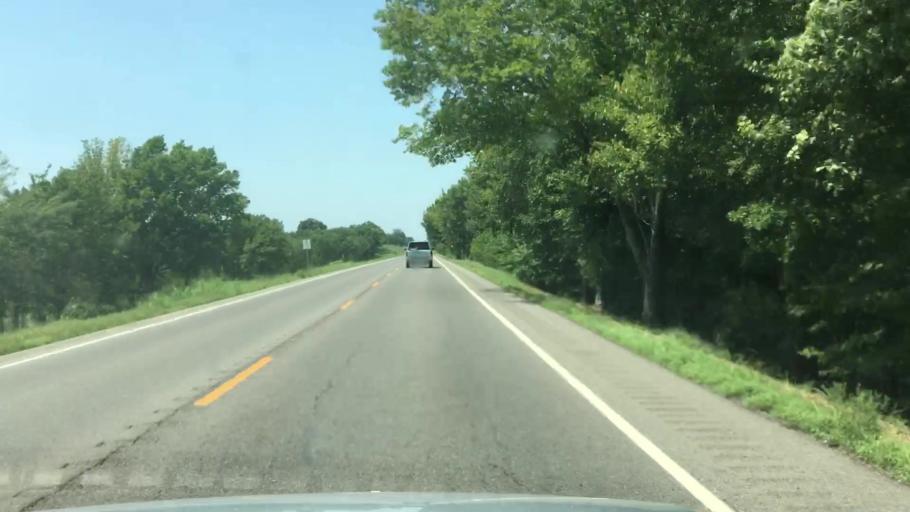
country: US
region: Oklahoma
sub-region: Wagoner County
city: Wagoner
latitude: 35.9371
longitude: -95.3338
